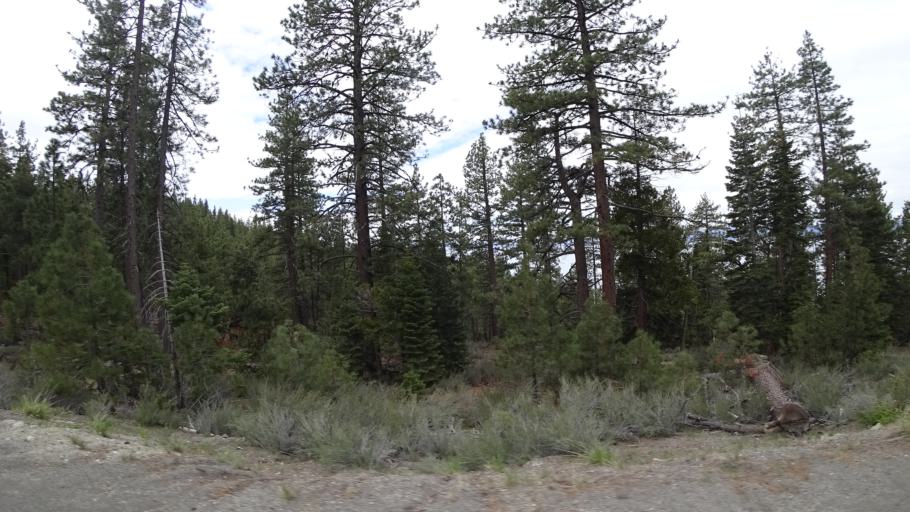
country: US
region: Nevada
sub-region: Washoe County
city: Incline Village
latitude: 39.1771
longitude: -119.9240
